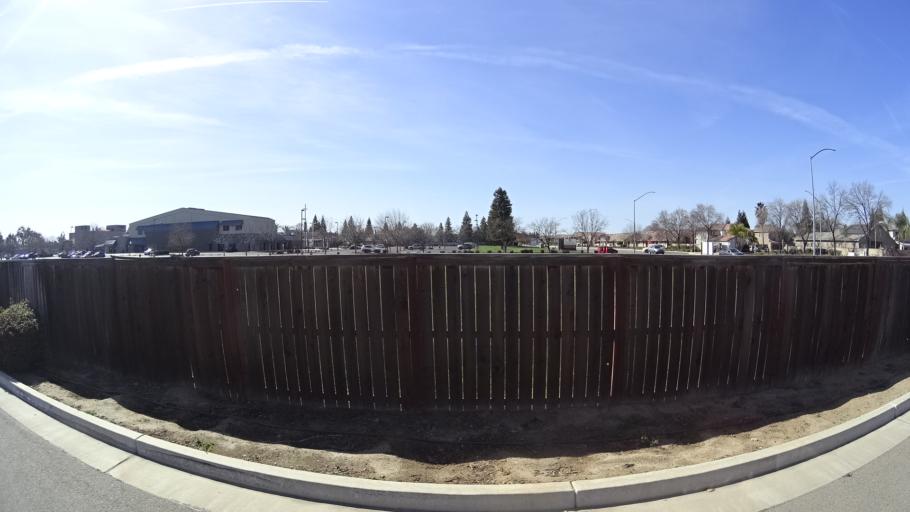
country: US
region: California
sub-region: Fresno County
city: Clovis
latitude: 36.8518
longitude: -119.7327
